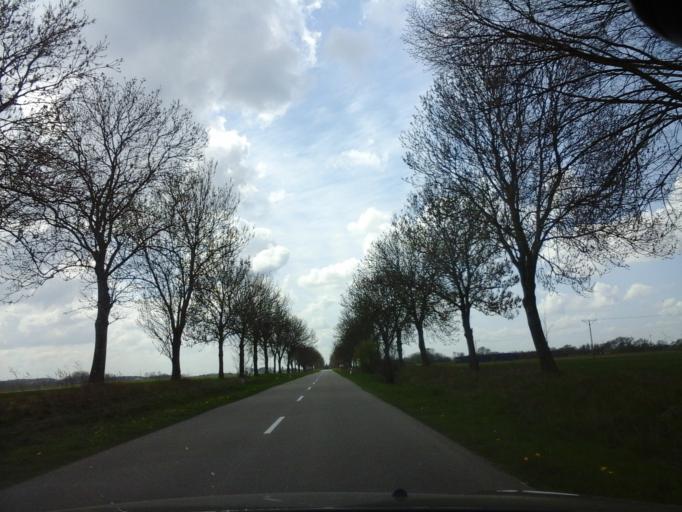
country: PL
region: West Pomeranian Voivodeship
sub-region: Powiat stargardzki
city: Suchan
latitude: 53.2892
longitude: 15.3456
